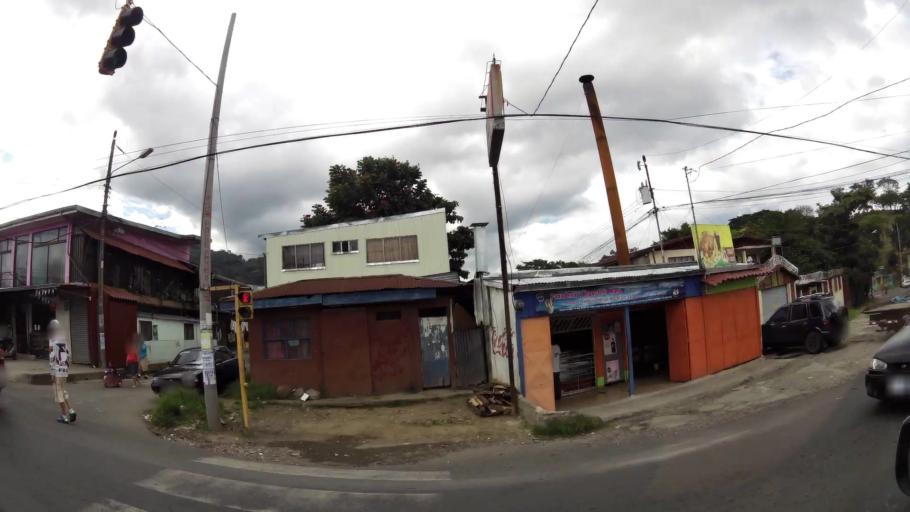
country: CR
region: San Jose
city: San Juan de Dios
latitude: 9.8849
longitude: -84.0841
